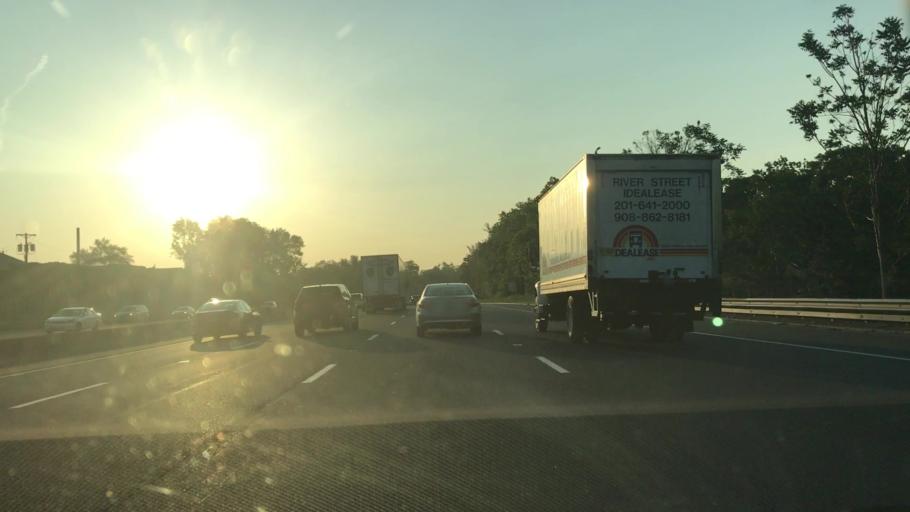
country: US
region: New Jersey
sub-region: Passaic County
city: Totowa
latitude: 40.8968
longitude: -74.2179
